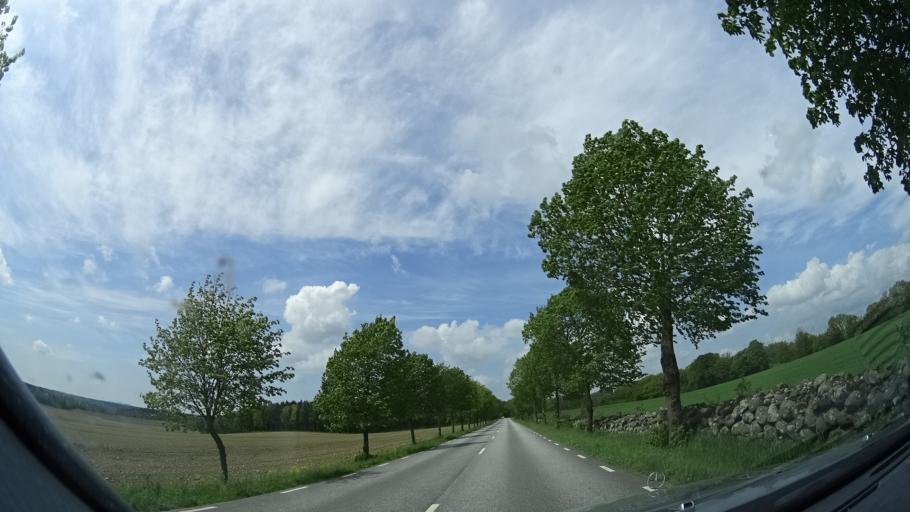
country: SE
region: Skane
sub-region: Sjobo Kommun
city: Sjoebo
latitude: 55.6807
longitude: 13.6460
